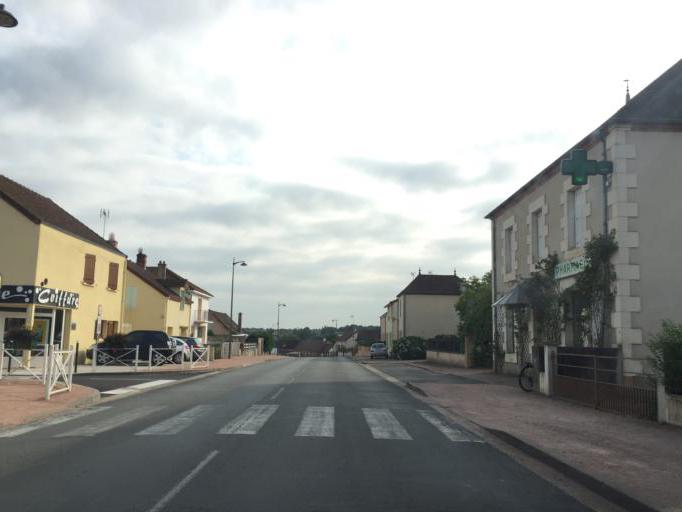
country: FR
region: Auvergne
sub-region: Departement de l'Allier
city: Molinet
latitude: 46.4654
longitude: 3.9358
